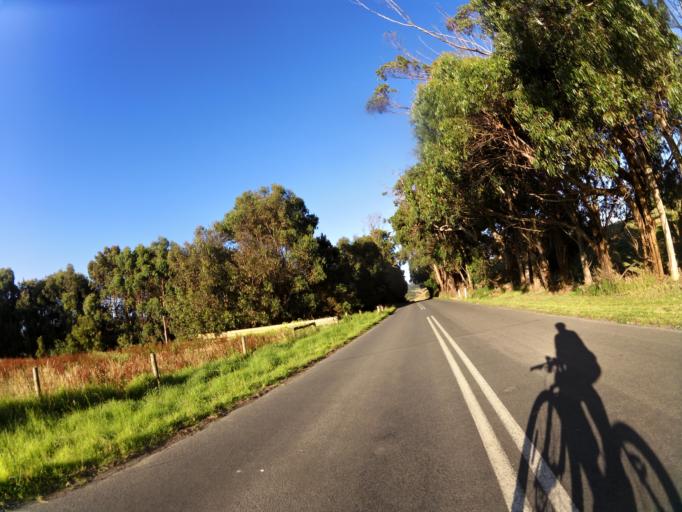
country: AU
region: Victoria
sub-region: Colac-Otway
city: Apollo Bay
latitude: -38.7673
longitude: 143.6551
